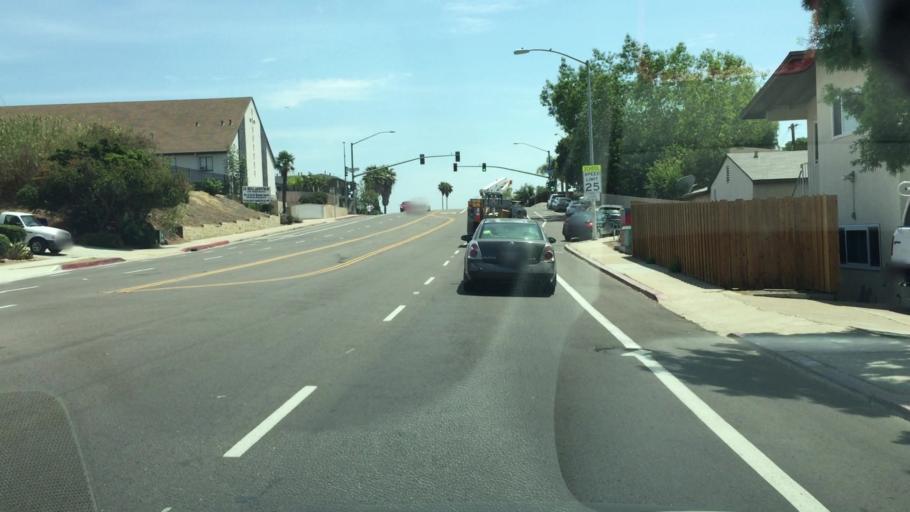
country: US
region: California
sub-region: San Diego County
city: Lemon Grove
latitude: 32.7589
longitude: -117.0664
